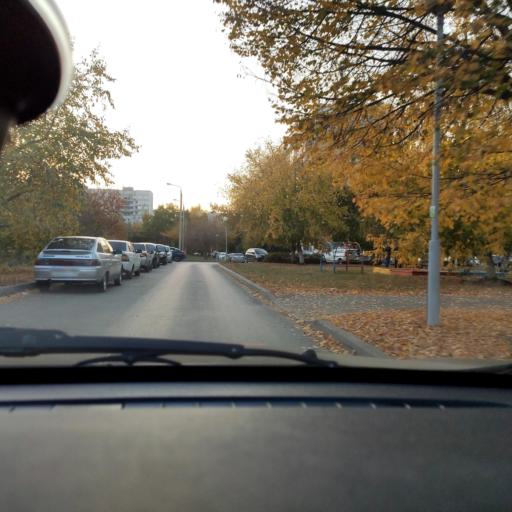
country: RU
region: Samara
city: Tol'yatti
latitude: 53.5360
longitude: 49.3342
